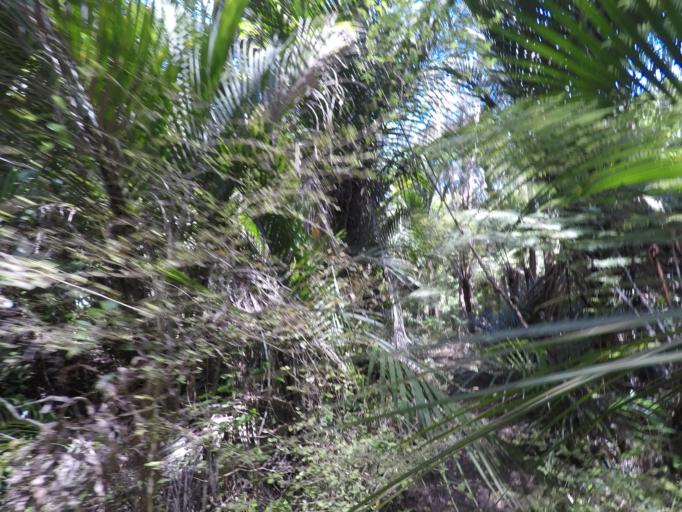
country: NZ
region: Auckland
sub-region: Auckland
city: Titirangi
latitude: -36.9740
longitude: 174.6308
